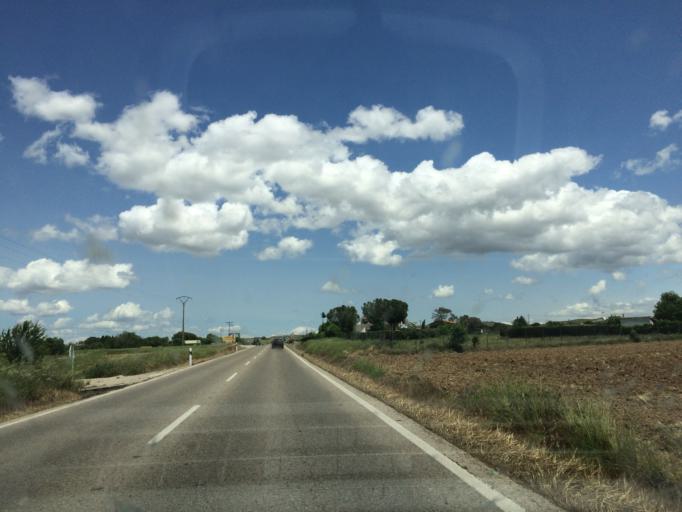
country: ES
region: Madrid
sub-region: Provincia de Madrid
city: Valdetorres de Jarama
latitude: 40.6634
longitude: -3.4842
